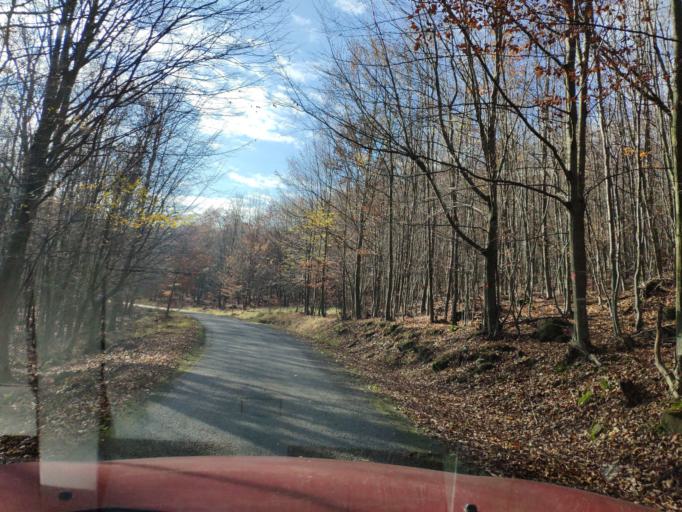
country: HU
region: Borsod-Abauj-Zemplen
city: Gonc
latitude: 48.6034
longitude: 21.4519
